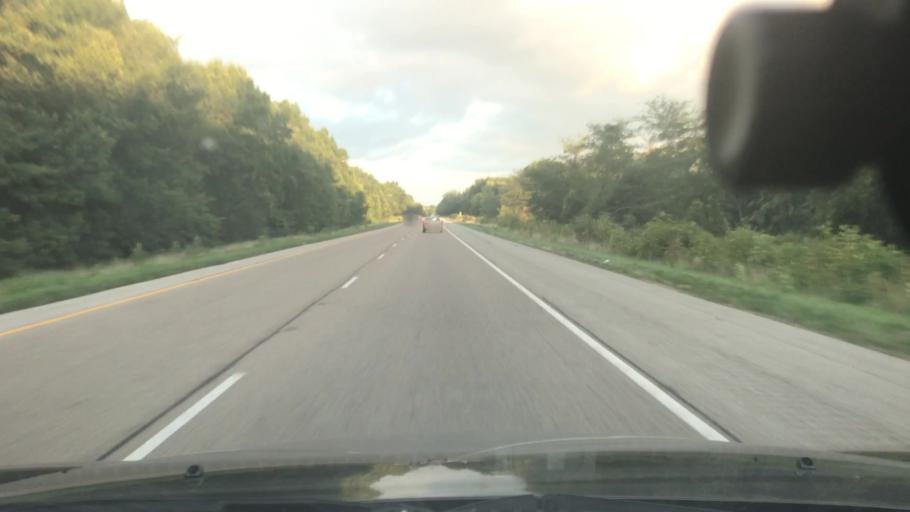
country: US
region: Illinois
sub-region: Clinton County
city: Albers
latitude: 38.4857
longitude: -89.5922
